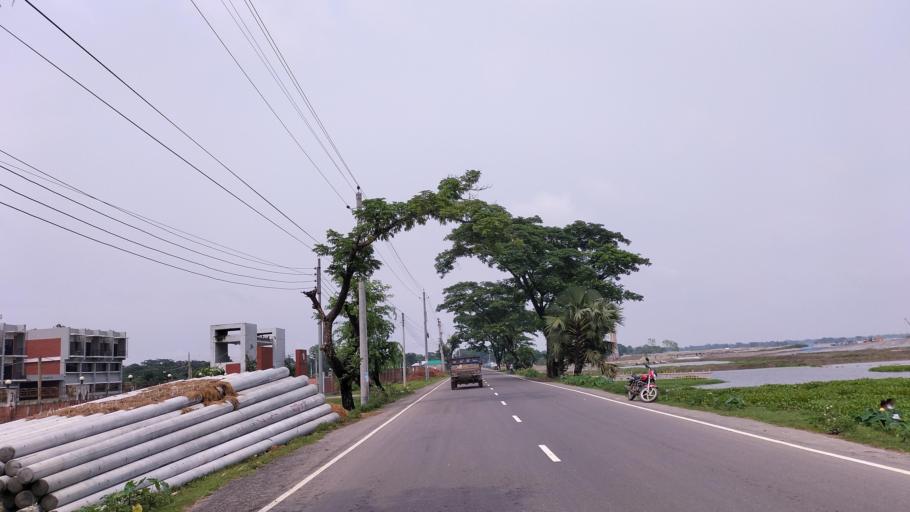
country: BD
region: Dhaka
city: Netrakona
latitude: 24.8981
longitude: 90.7486
